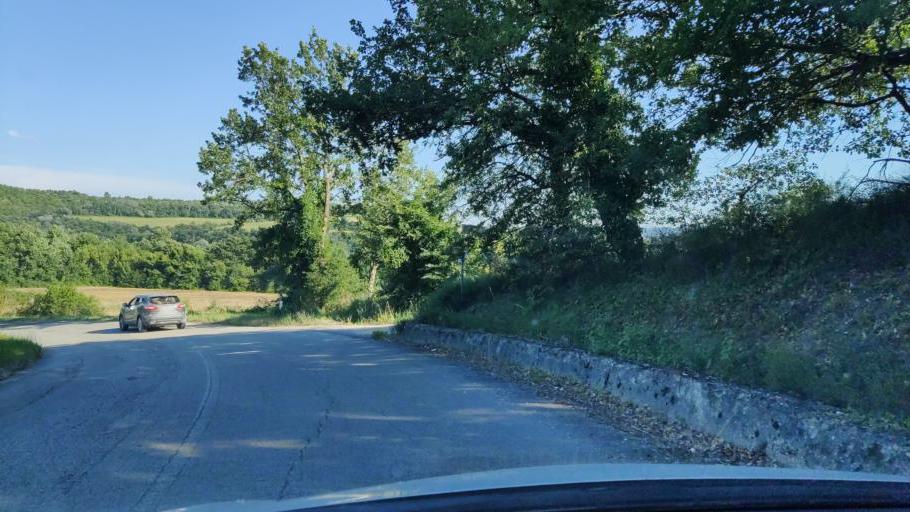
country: IT
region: Umbria
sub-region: Provincia di Terni
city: Penna in Teverina
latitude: 42.4838
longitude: 12.3673
